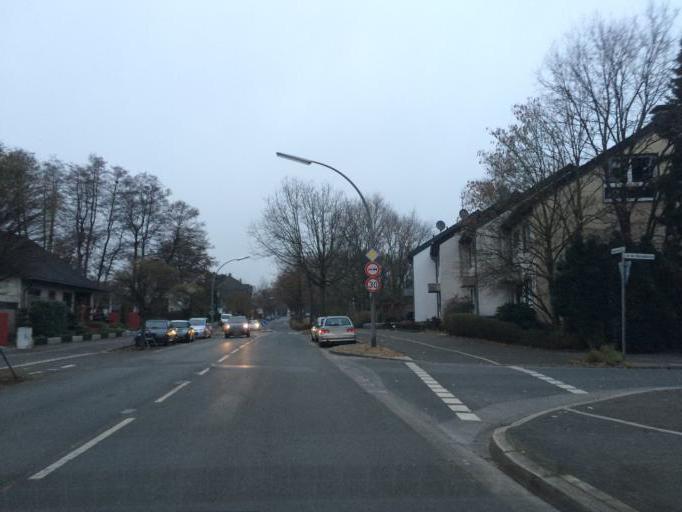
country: DE
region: North Rhine-Westphalia
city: Dorsten
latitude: 51.6761
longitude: 6.9727
